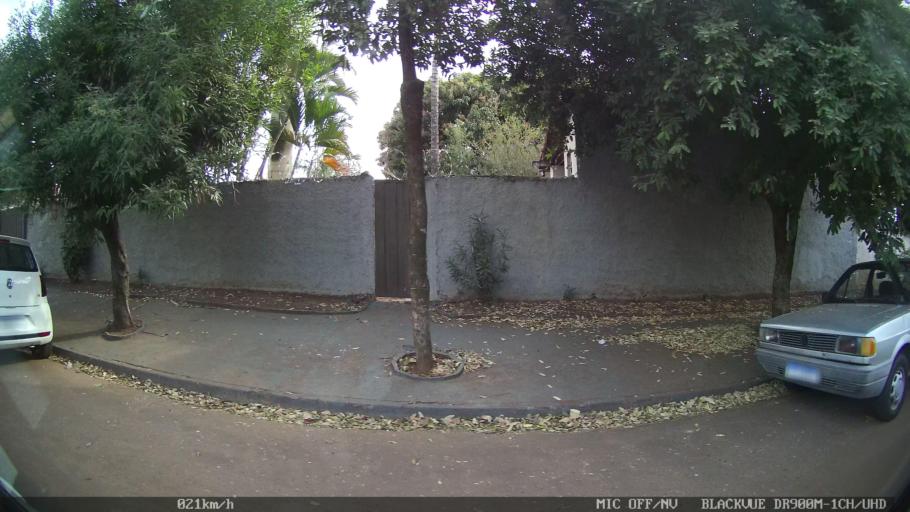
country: BR
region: Sao Paulo
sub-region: Catanduva
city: Catanduva
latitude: -21.1379
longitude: -48.9970
